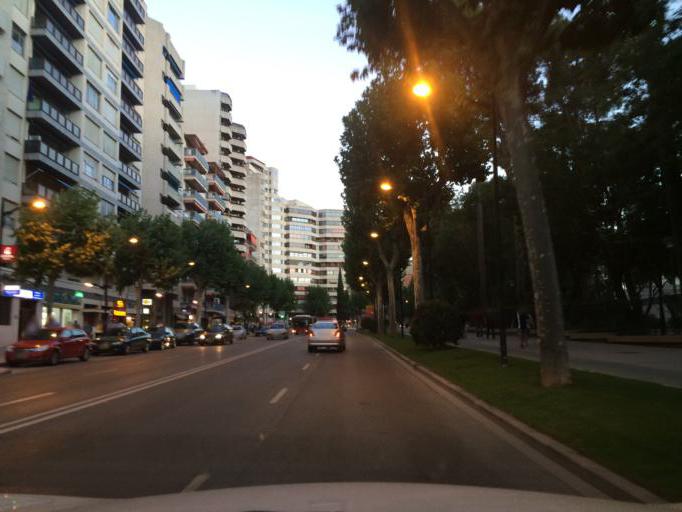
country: ES
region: Castille-La Mancha
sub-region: Provincia de Albacete
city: Albacete
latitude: 38.9883
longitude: -1.8552
